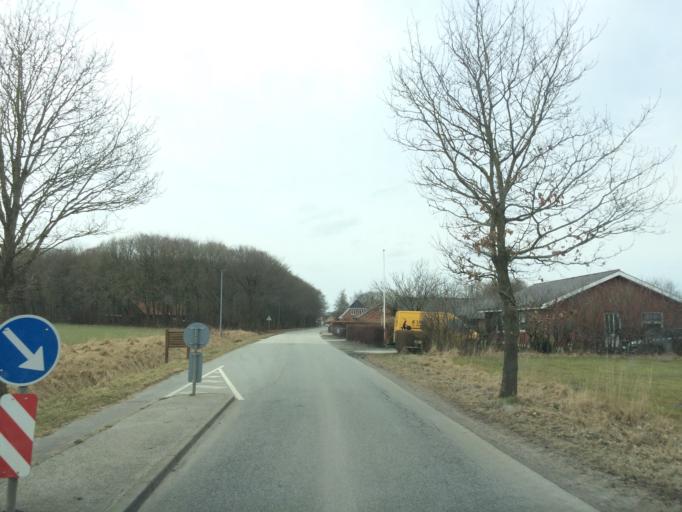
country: DK
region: Central Jutland
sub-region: Ringkobing-Skjern Kommune
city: Tarm
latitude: 55.8236
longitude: 8.4157
